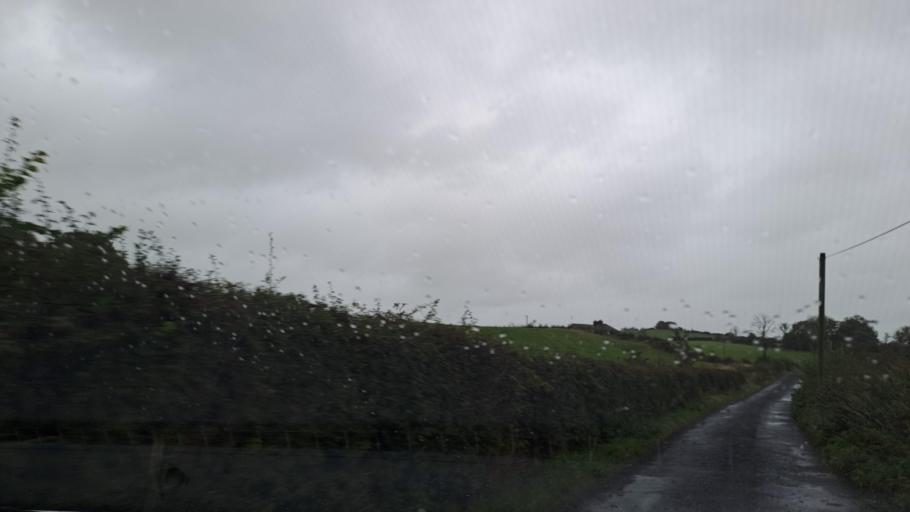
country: IE
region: Ulster
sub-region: An Cabhan
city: Kingscourt
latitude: 54.0071
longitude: -6.8367
